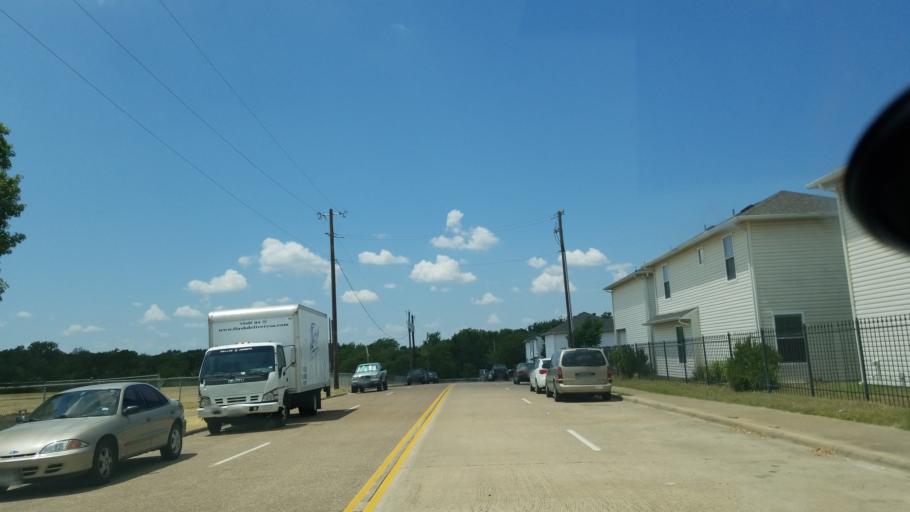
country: US
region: Texas
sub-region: Dallas County
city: Cockrell Hill
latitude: 32.7166
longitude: -96.9010
